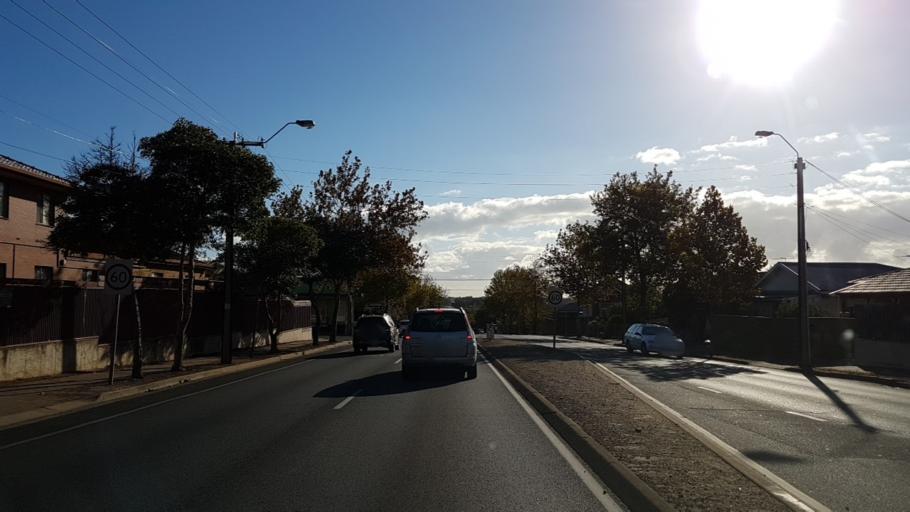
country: AU
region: South Australia
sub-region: Prospect
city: Prospect
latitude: -34.8741
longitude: 138.5954
